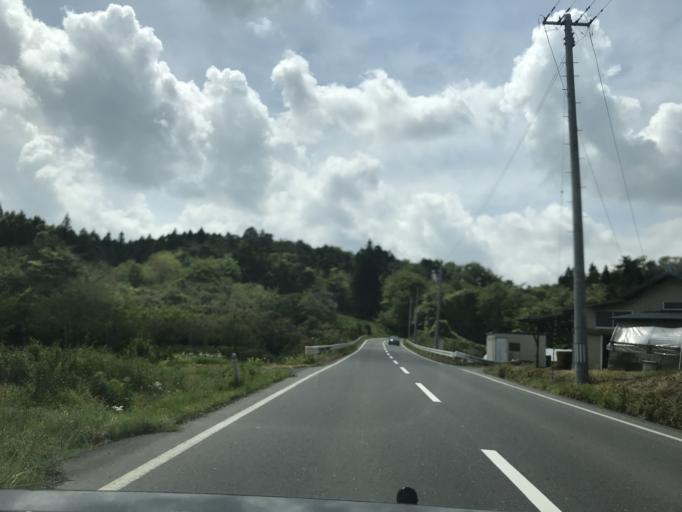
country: JP
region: Iwate
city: Ichinoseki
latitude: 38.7863
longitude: 141.0007
